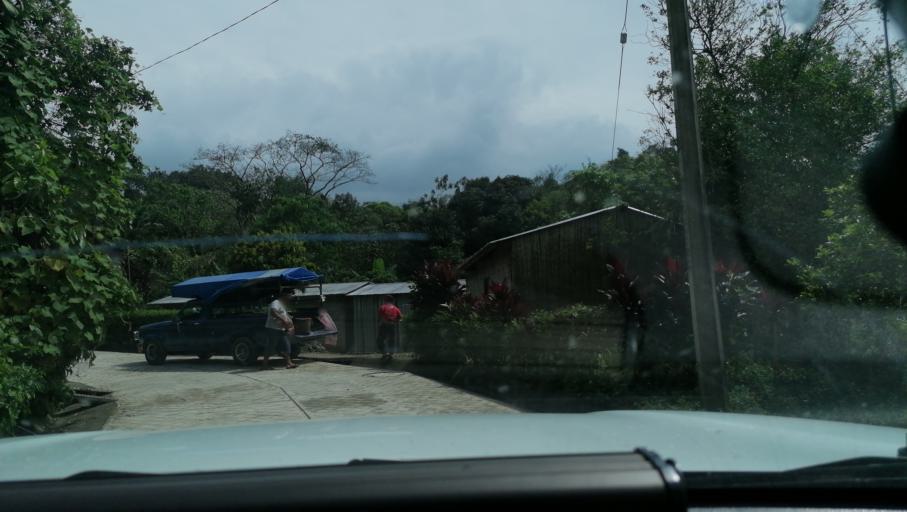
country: MX
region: Chiapas
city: Ocotepec
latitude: 17.3077
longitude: -93.1815
